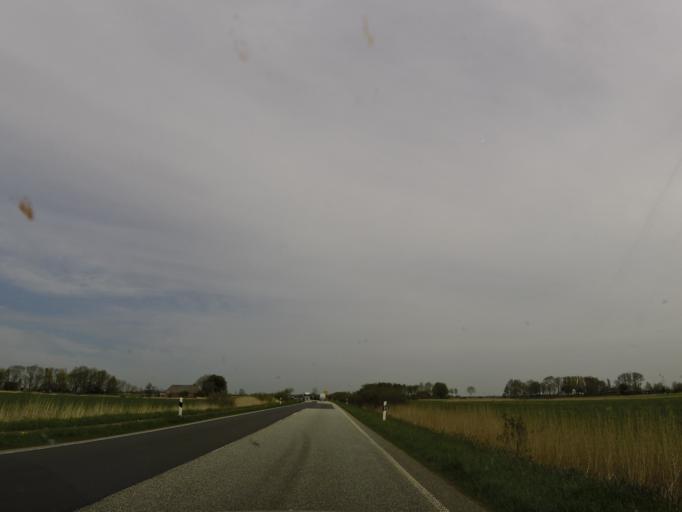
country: DE
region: Schleswig-Holstein
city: Koldenbuttel
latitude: 54.4169
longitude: 9.0474
